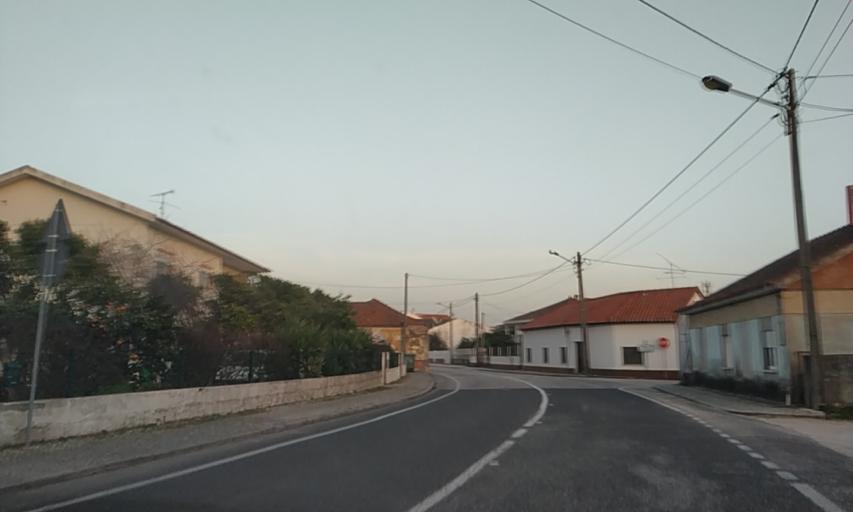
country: PT
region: Leiria
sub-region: Marinha Grande
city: Marinha Grande
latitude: 39.7464
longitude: -8.9464
